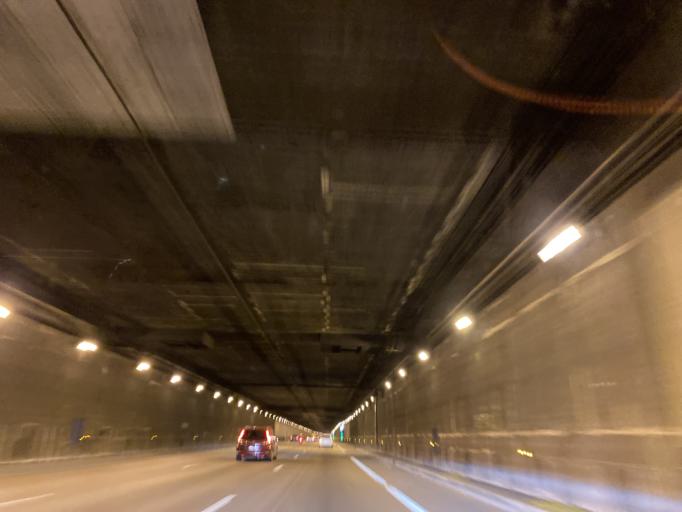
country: FR
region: Ile-de-France
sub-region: Departement des Hauts-de-Seine
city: Nanterre
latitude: 48.8988
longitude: 2.2152
